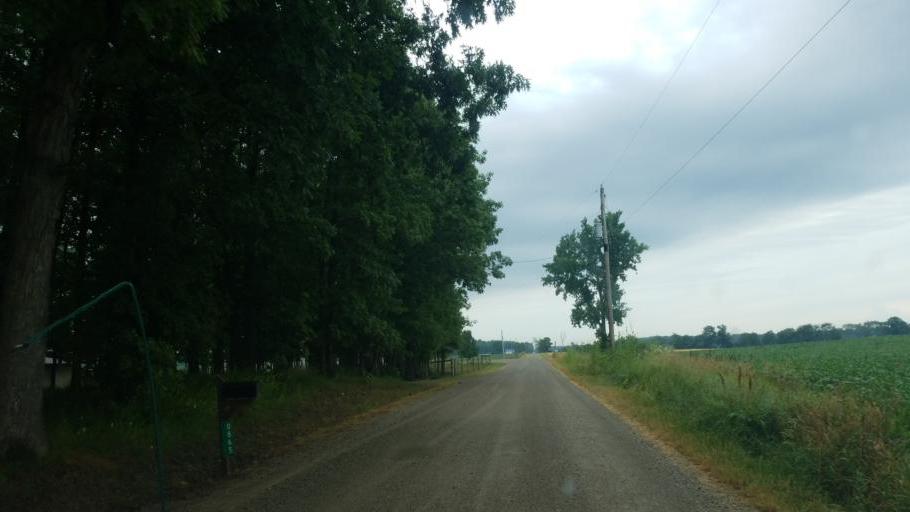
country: US
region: Indiana
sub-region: Steuben County
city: Hamilton
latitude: 41.5017
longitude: -84.9112
